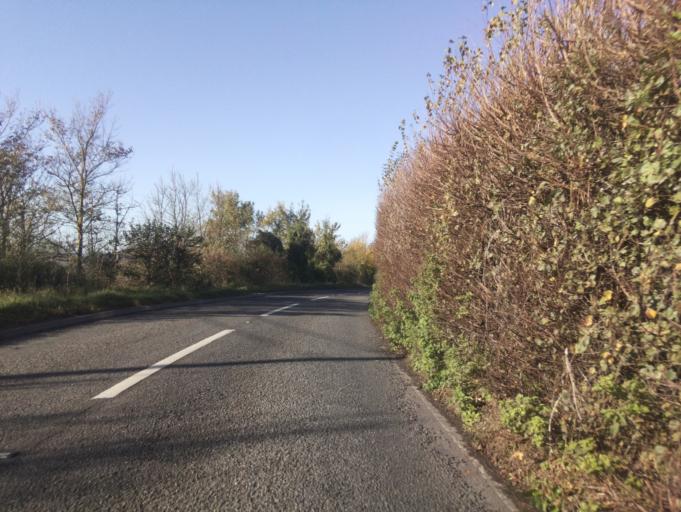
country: GB
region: England
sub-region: Somerset
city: Langport
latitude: 51.0515
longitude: -2.8357
